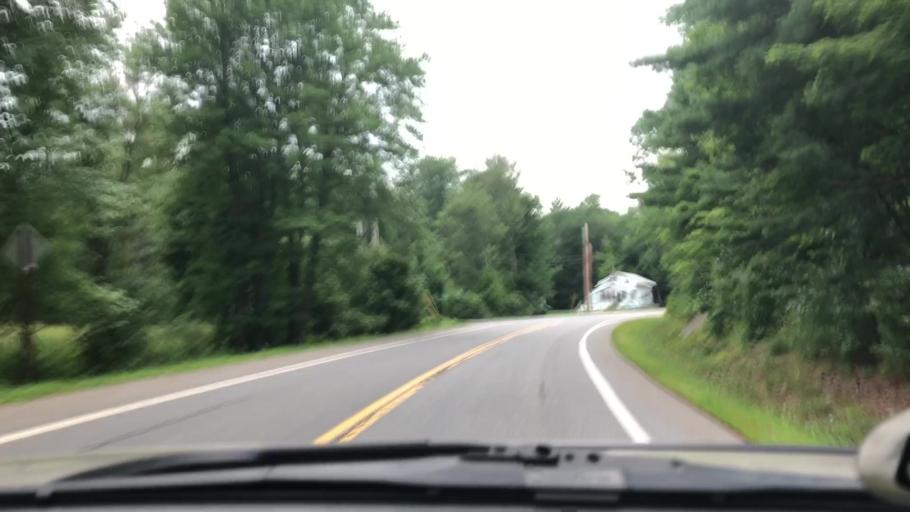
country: US
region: New York
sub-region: Saratoga County
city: Corinth
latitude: 43.2100
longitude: -73.7912
